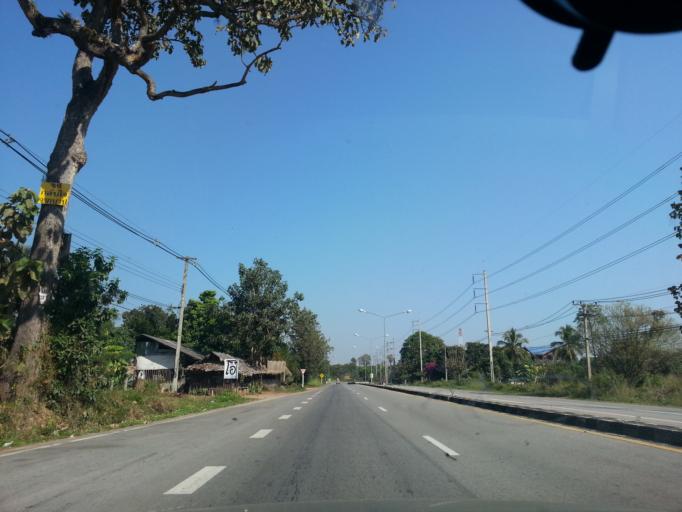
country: TH
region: Chiang Mai
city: Mae Taeng
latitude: 19.1704
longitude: 98.9488
